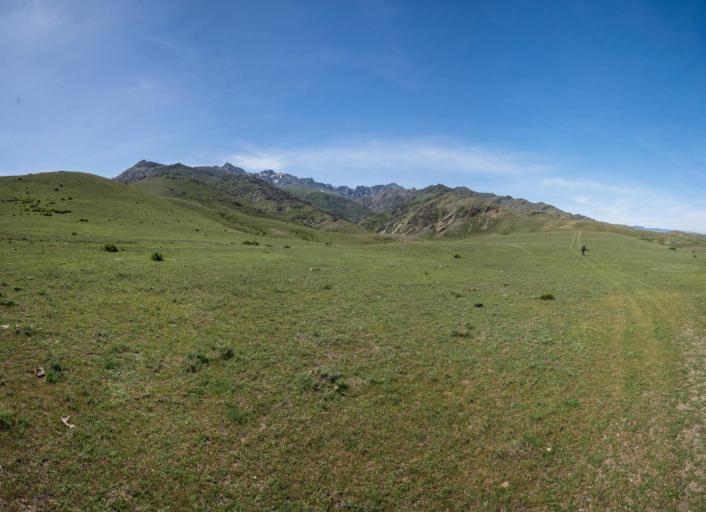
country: KZ
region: Ongtustik Qazaqstan
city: Khantaghy
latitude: 43.8467
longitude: 68.6738
